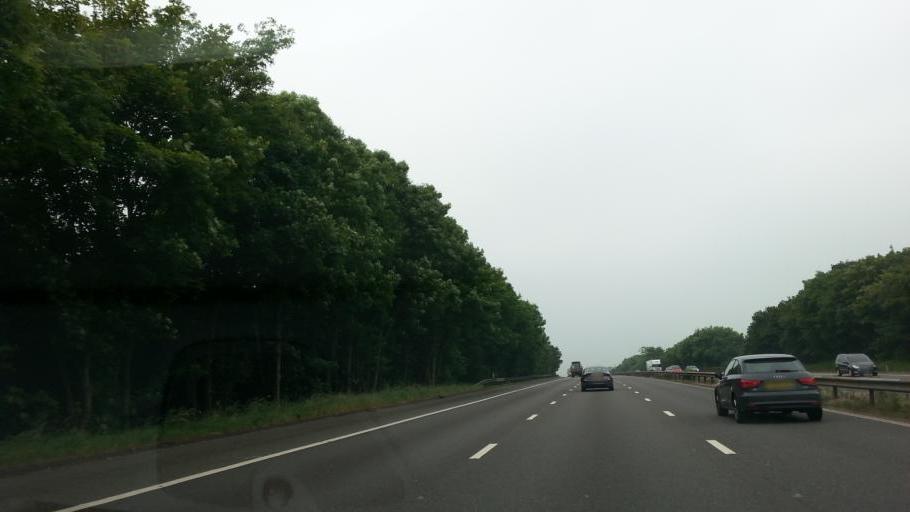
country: GB
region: England
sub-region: Warwickshire
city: Bedworth
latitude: 52.4644
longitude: -1.4104
